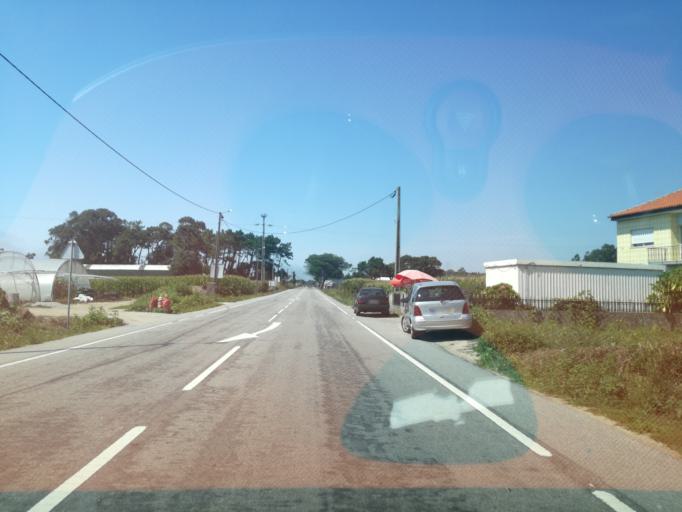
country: PT
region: Braga
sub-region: Esposende
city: Apulia
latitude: 41.4956
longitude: -8.7563
